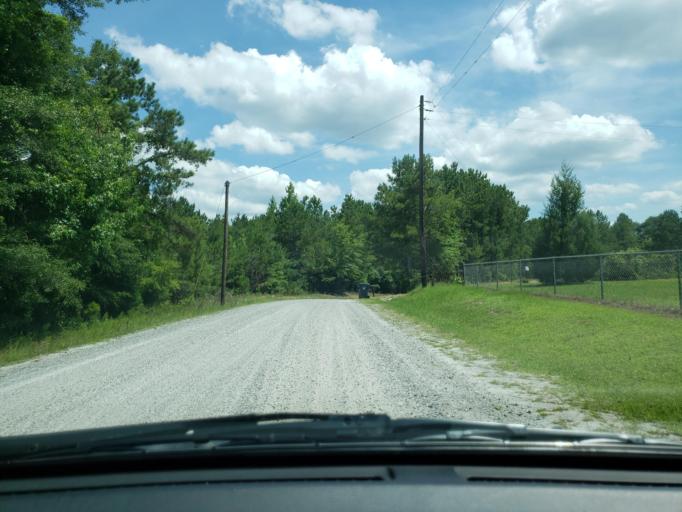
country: US
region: Alabama
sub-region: Elmore County
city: Eclectic
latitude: 32.6239
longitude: -85.9455
